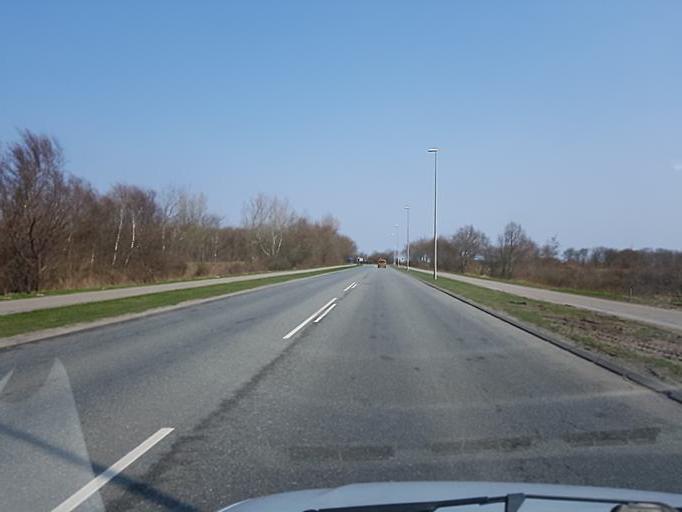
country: DK
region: South Denmark
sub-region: Esbjerg Kommune
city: Esbjerg
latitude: 55.4949
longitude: 8.4664
